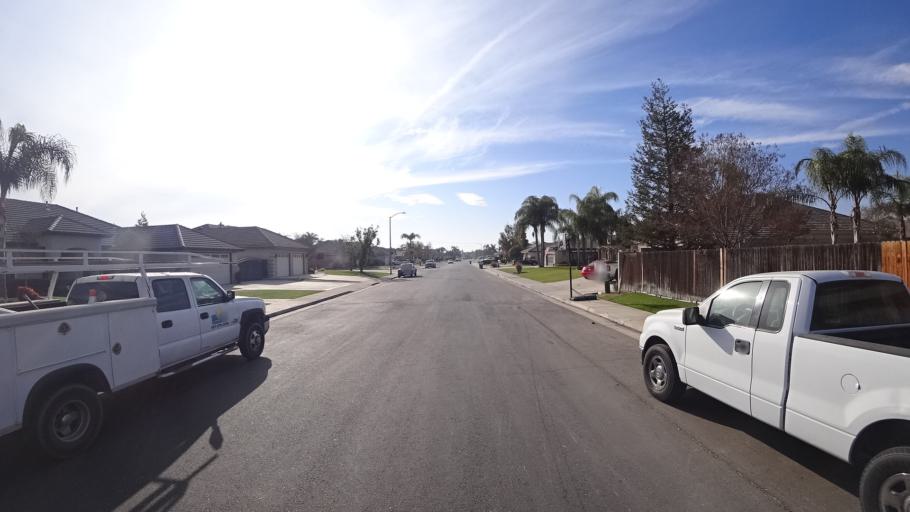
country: US
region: California
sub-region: Kern County
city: Rosedale
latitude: 35.4073
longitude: -119.1417
